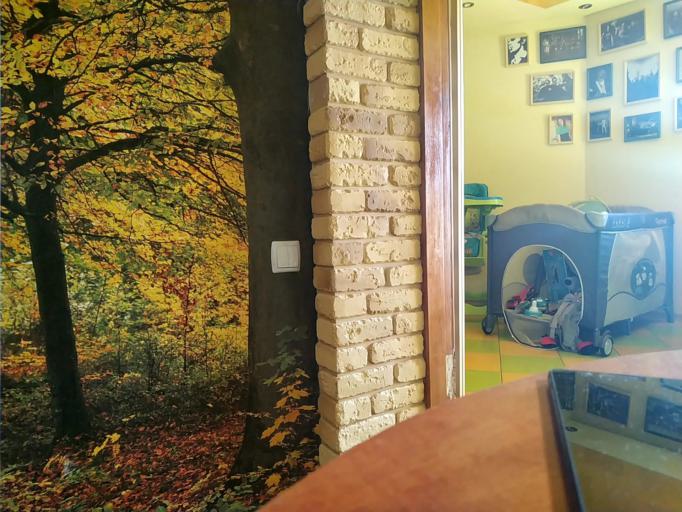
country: RU
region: Tverskaya
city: Vyshniy Volochek
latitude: 57.5151
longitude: 34.6360
